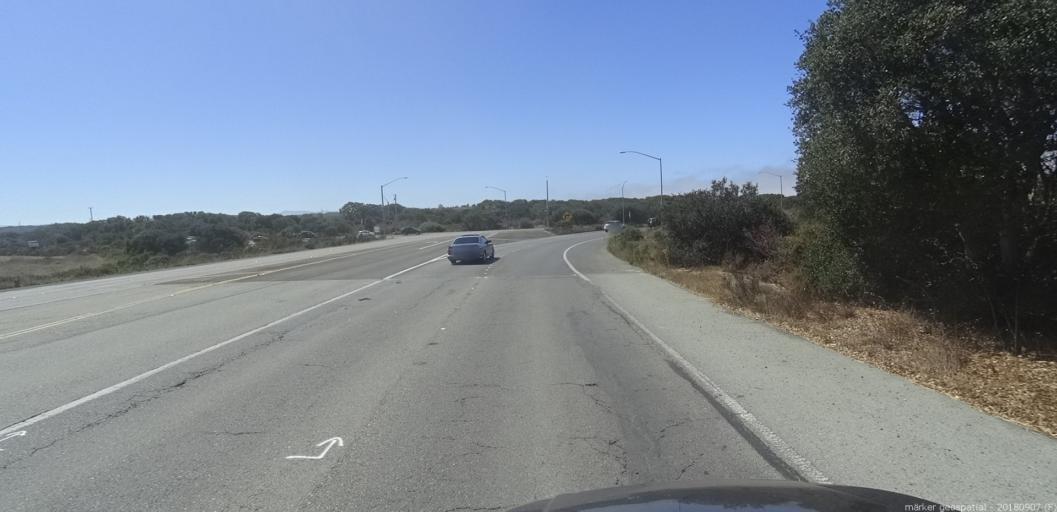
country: US
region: California
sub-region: Monterey County
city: Marina
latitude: 36.6681
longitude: -121.7561
